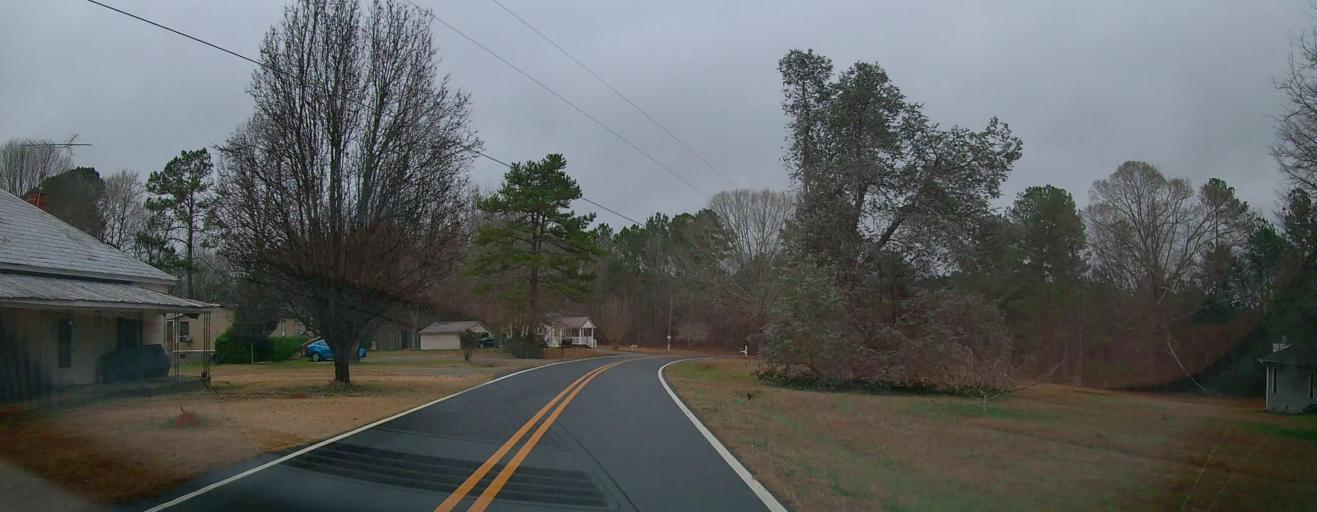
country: US
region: Georgia
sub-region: Monroe County
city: Forsyth
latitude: 33.0639
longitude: -83.8903
